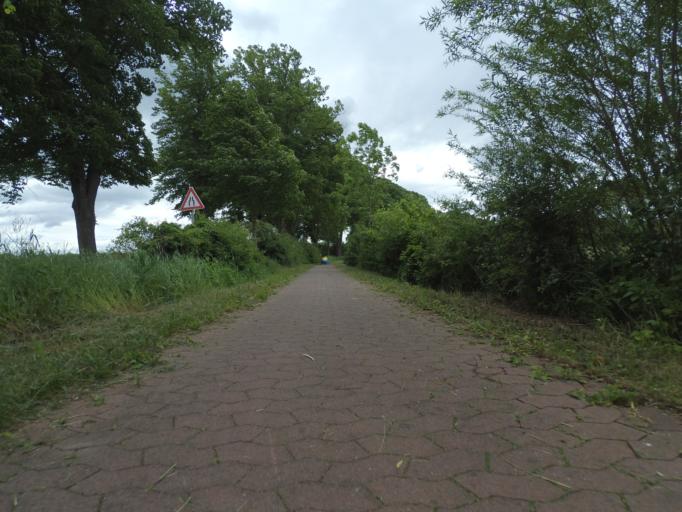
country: DE
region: Lower Saxony
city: Gross Munzel
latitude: 52.4241
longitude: 9.4993
